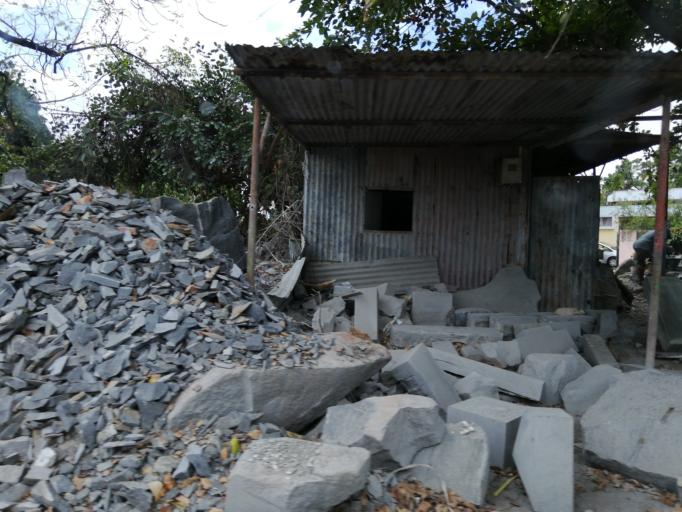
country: MU
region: Port Louis
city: Port Louis
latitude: -20.1617
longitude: 57.4871
